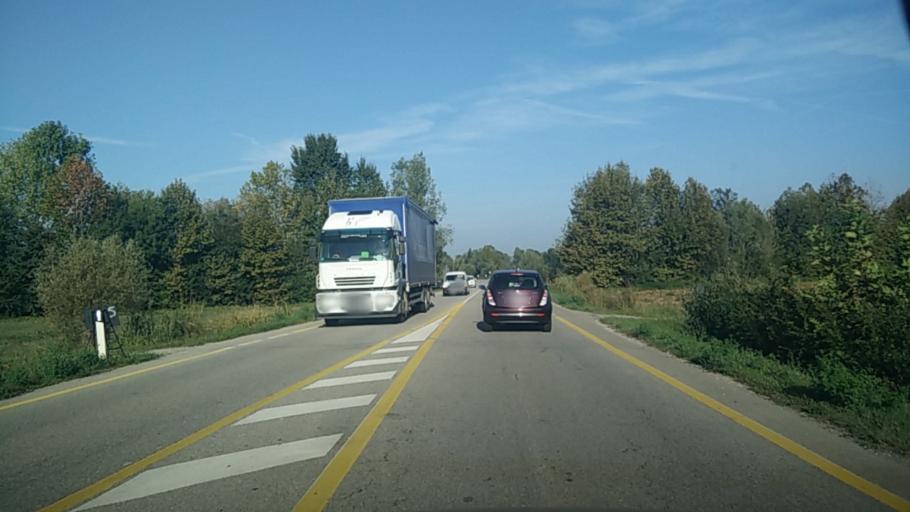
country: IT
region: Veneto
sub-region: Provincia di Padova
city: Piombino Dese
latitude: 45.6172
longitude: 11.9908
